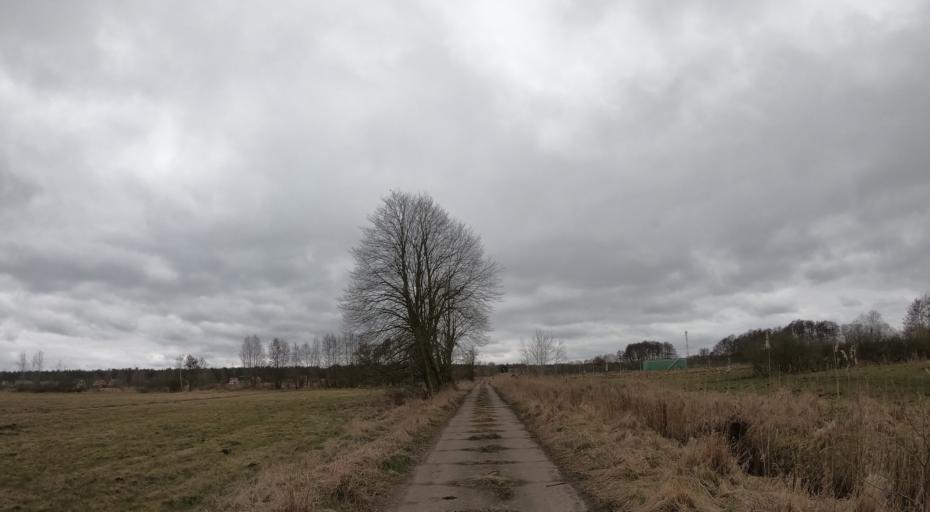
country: PL
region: West Pomeranian Voivodeship
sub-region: Powiat policki
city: Nowe Warpno
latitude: 53.6794
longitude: 14.3866
